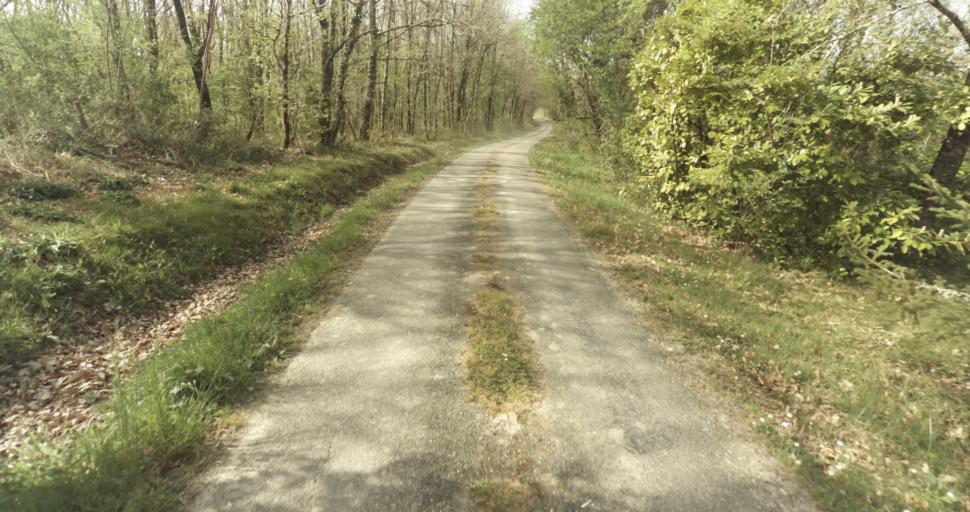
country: FR
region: Midi-Pyrenees
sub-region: Departement du Tarn-et-Garonne
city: Lafrancaise
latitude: 44.1504
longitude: 1.1784
